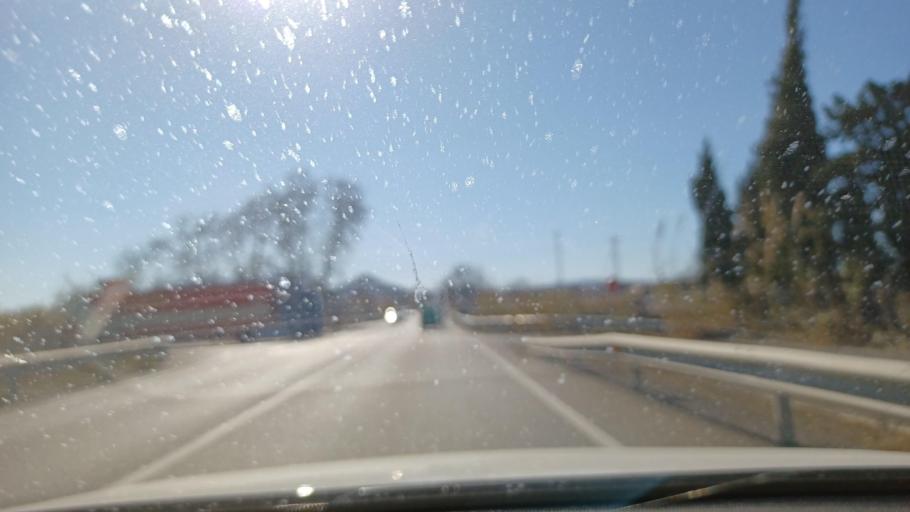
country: ES
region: Catalonia
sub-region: Provincia de Tarragona
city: Amposta
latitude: 40.7196
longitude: 0.5866
